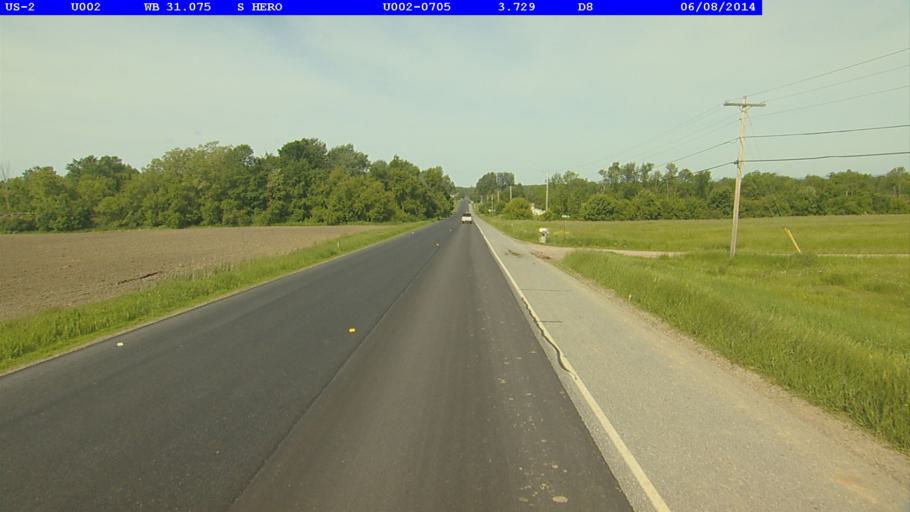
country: US
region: New York
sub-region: Clinton County
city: Cumberland Head
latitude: 44.6470
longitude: -73.2896
